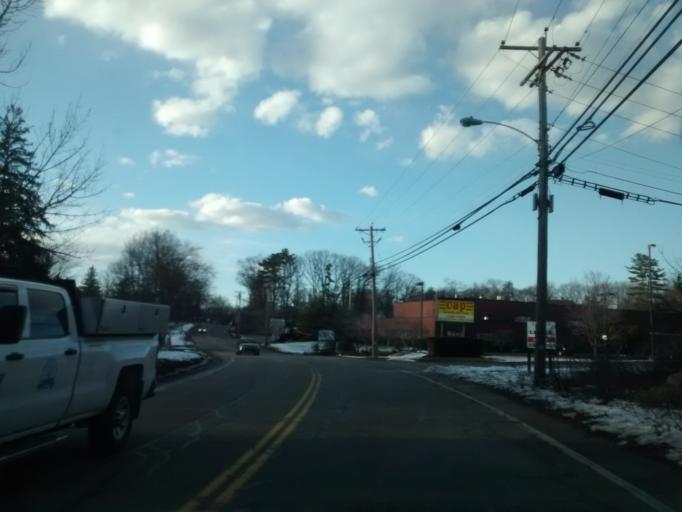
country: US
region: Massachusetts
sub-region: Worcester County
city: Milford
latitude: 42.1588
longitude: -71.5070
